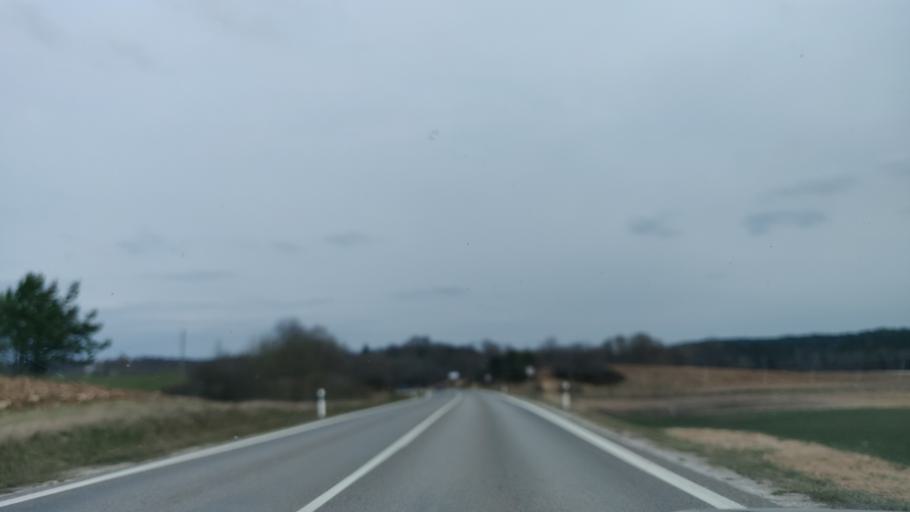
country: LT
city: Aukstadvaris
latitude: 54.5761
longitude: 24.5077
